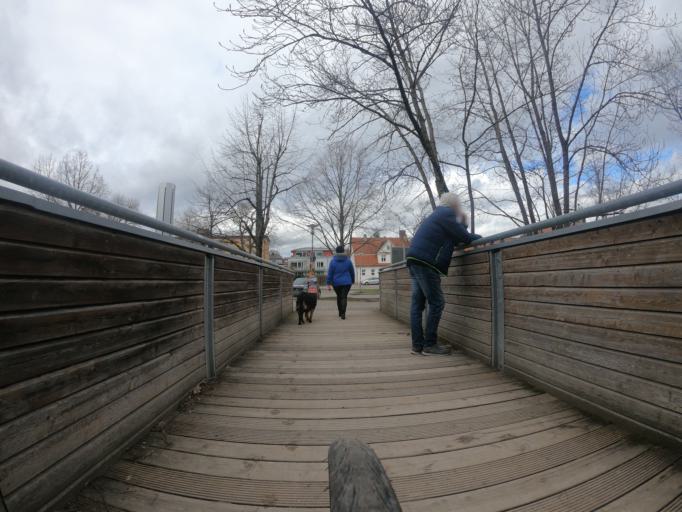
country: DE
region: Bavaria
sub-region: Upper Bavaria
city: Fuerstenfeldbruck
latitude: 48.1747
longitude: 11.2500
